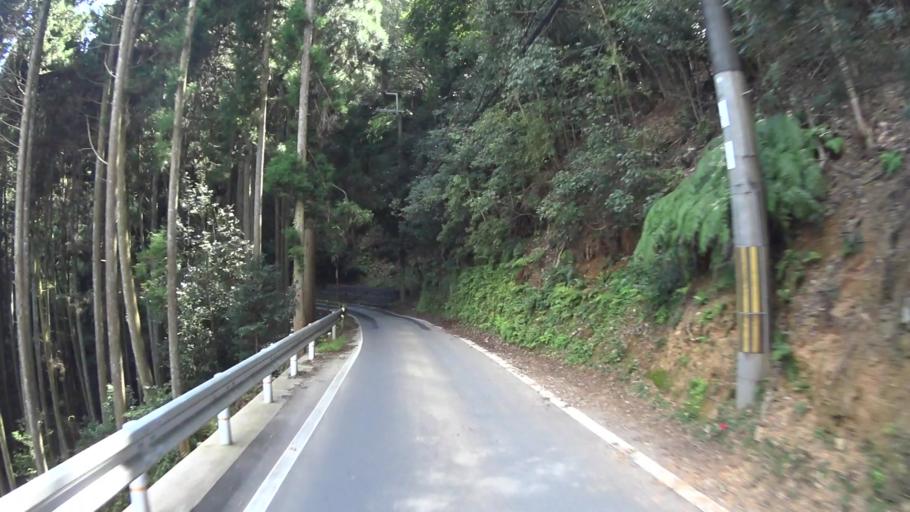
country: JP
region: Kyoto
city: Uji
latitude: 34.9151
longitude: 135.8504
